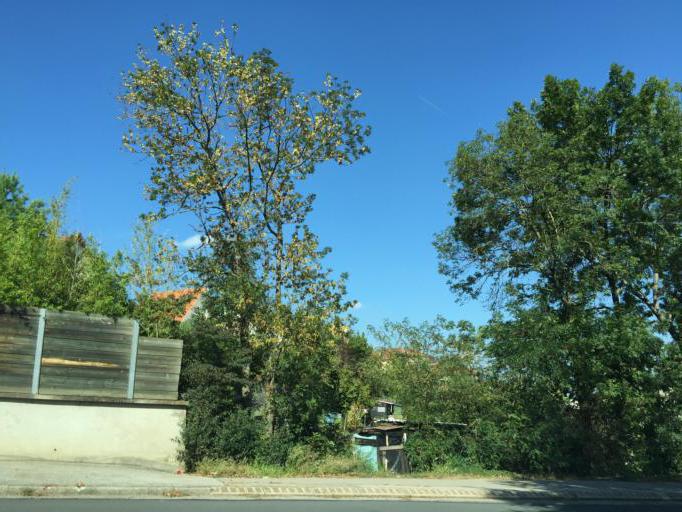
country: FR
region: Rhone-Alpes
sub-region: Departement de la Loire
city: La Grand-Croix
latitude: 45.4833
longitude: 4.5438
